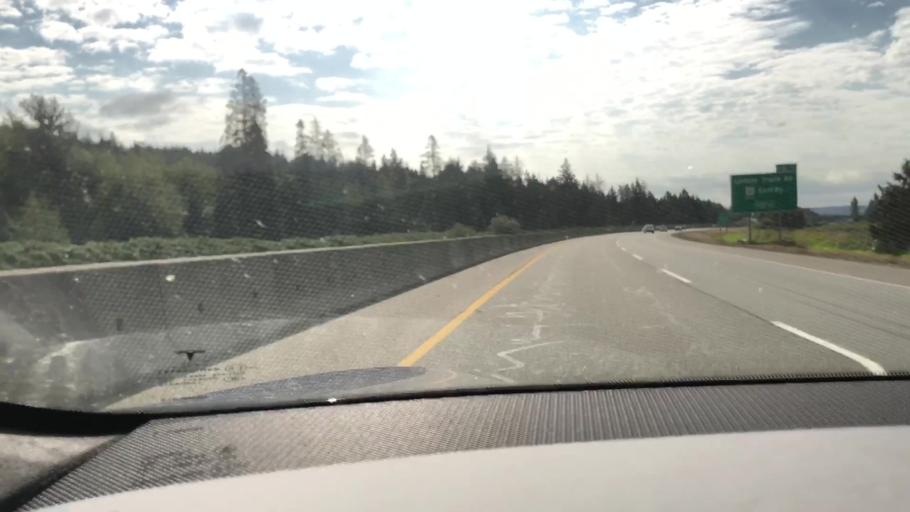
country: CA
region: British Columbia
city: Delta
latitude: 49.1111
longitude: -122.9067
